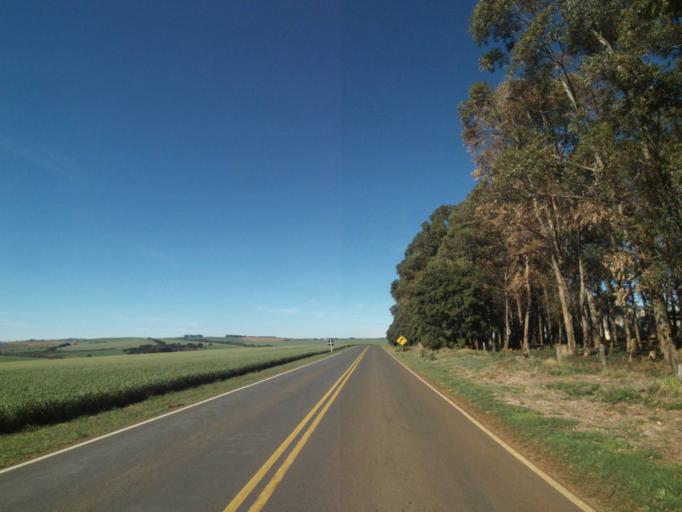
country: BR
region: Parana
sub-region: Tibagi
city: Tibagi
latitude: -24.5529
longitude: -50.2911
